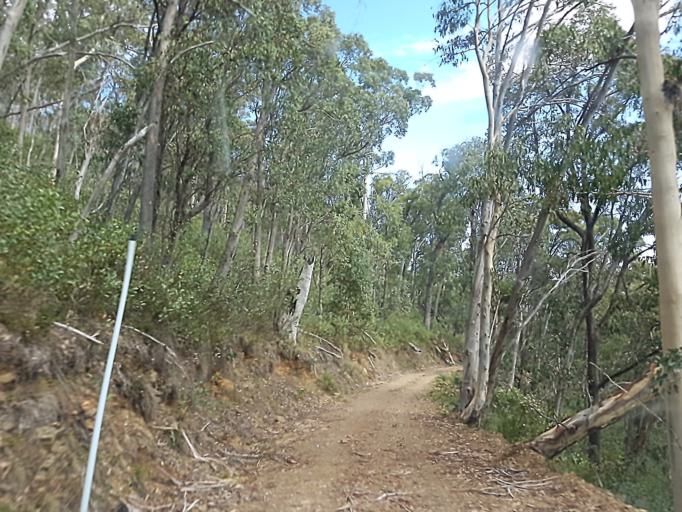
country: AU
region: Victoria
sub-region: Alpine
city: Mount Beauty
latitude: -36.9108
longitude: 147.0014
